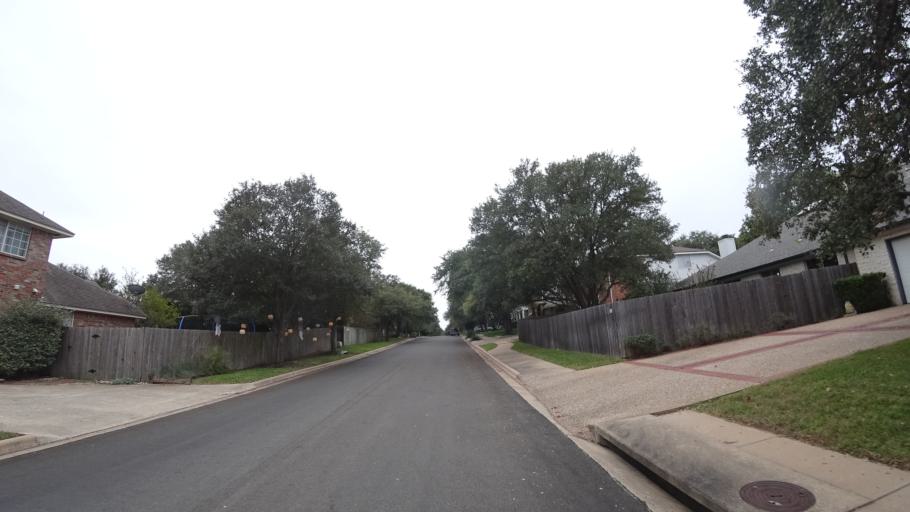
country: US
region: Texas
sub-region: Travis County
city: Shady Hollow
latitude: 30.1879
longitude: -97.8923
